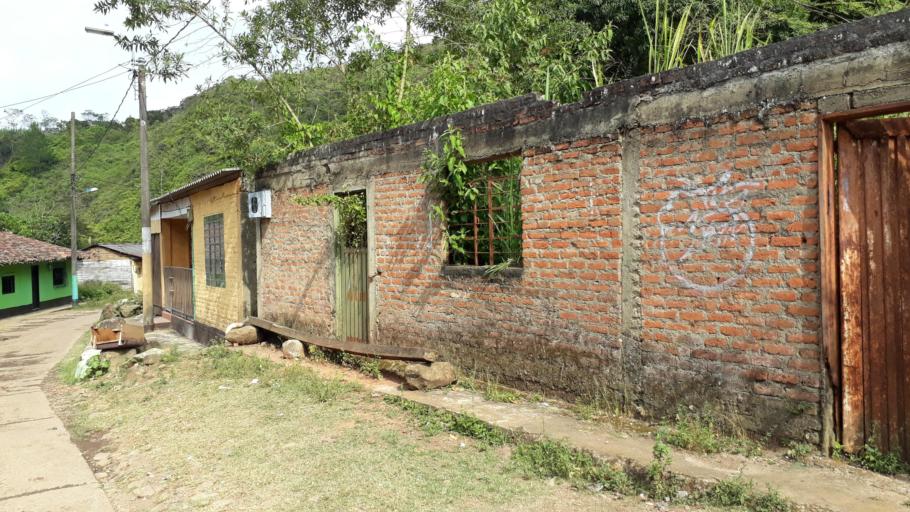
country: CO
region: Valle del Cauca
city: Jamundi
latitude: 3.2222
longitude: -76.6287
